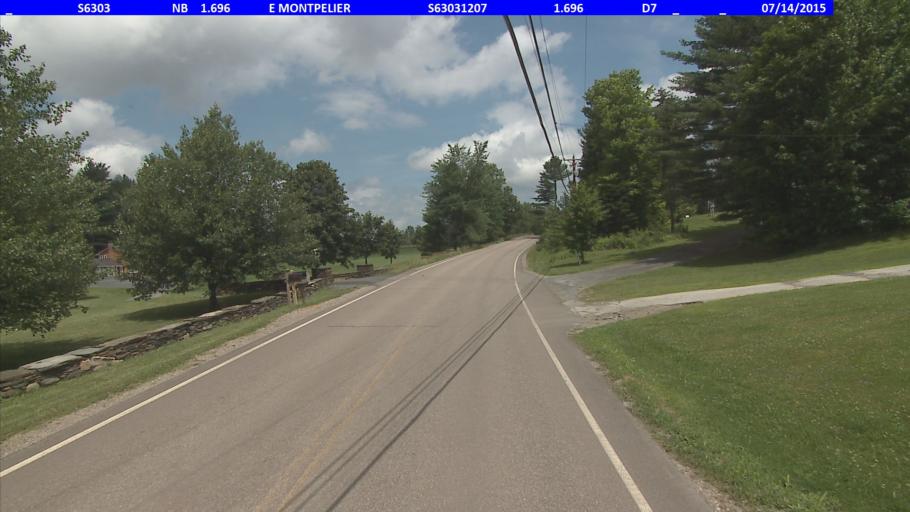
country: US
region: Vermont
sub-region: Washington County
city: Montpelier
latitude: 44.2933
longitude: -72.5393
